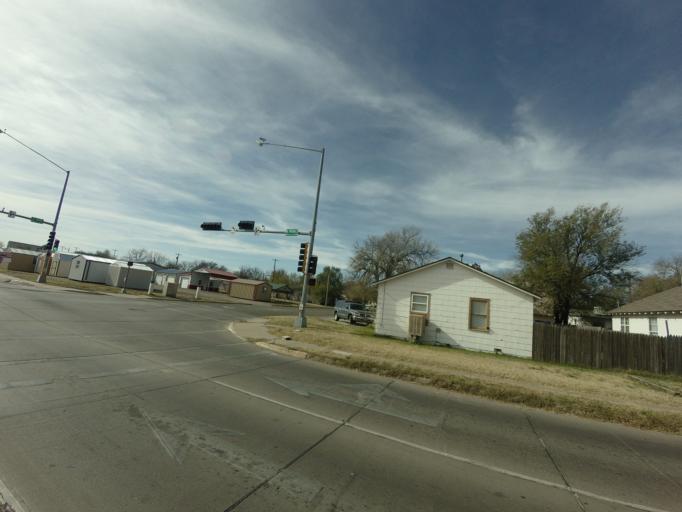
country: US
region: New Mexico
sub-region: Curry County
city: Clovis
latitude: 34.4080
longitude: -103.1965
